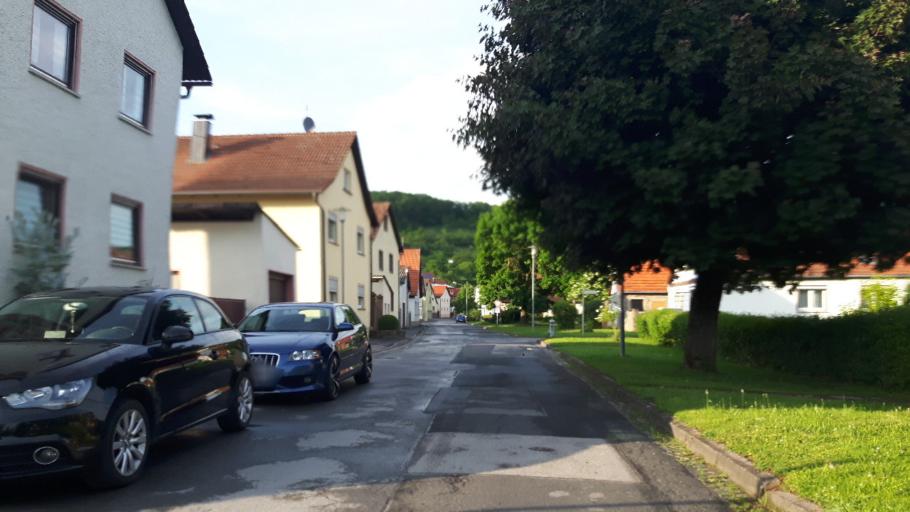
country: DE
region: Bavaria
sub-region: Regierungsbezirk Unterfranken
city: Sulzfeld
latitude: 50.2274
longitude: 10.4060
